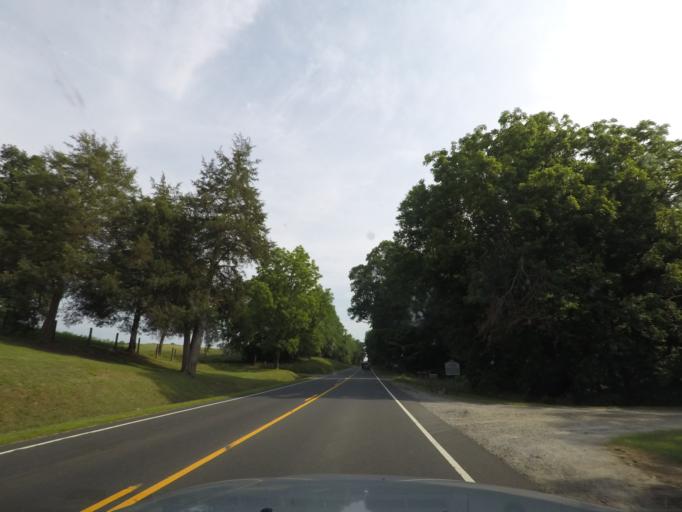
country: US
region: Virginia
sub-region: Prince Edward County
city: Hampden Sydney
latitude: 37.2183
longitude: -78.4424
